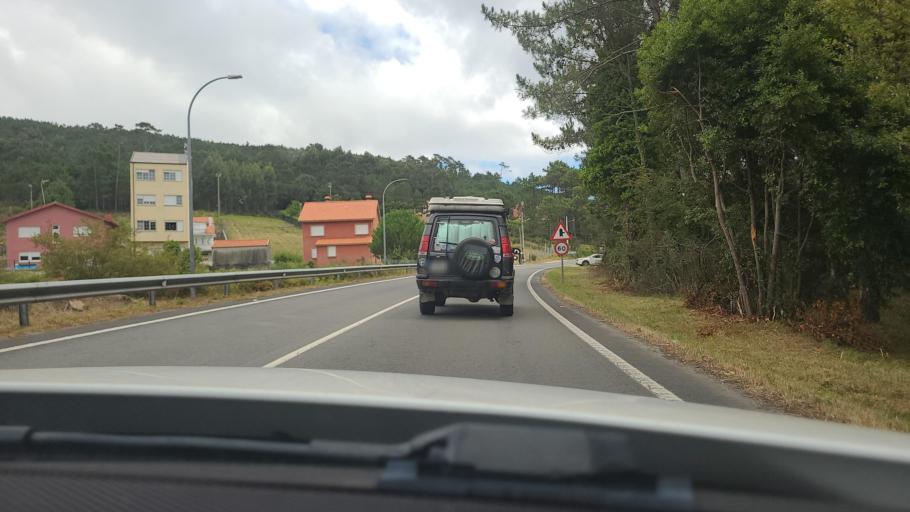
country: ES
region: Galicia
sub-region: Provincia da Coruna
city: Fisterra
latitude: 42.9285
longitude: -9.2559
